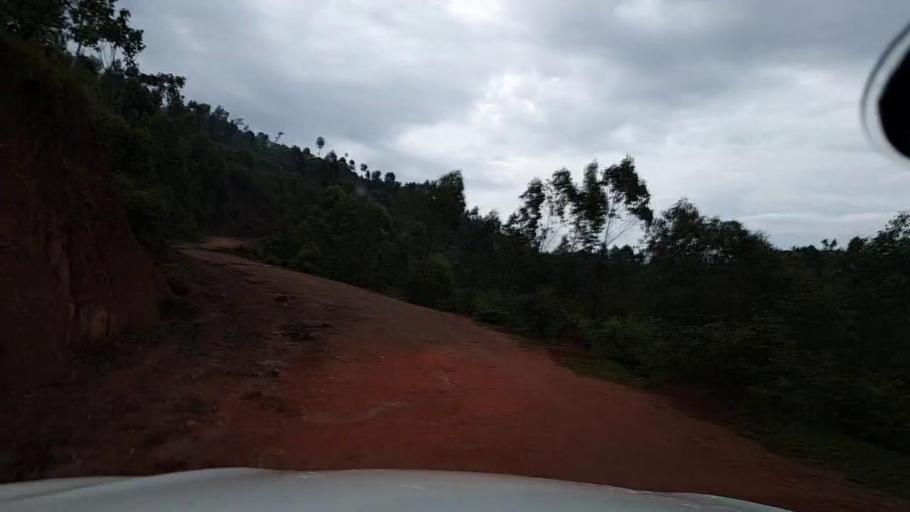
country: BI
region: Kayanza
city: Kayanza
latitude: -2.7202
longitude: 29.5457
